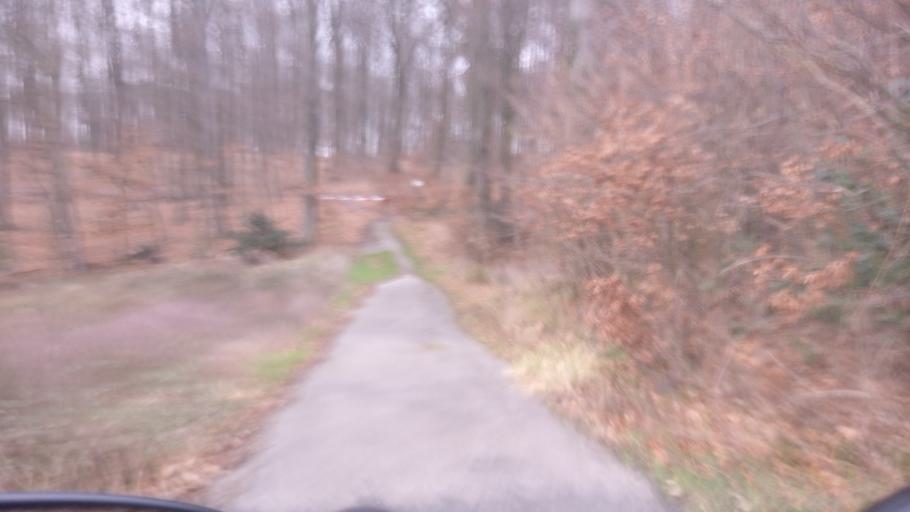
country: DE
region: North Rhine-Westphalia
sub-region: Regierungsbezirk Detmold
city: Lage
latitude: 52.0024
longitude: 8.7817
